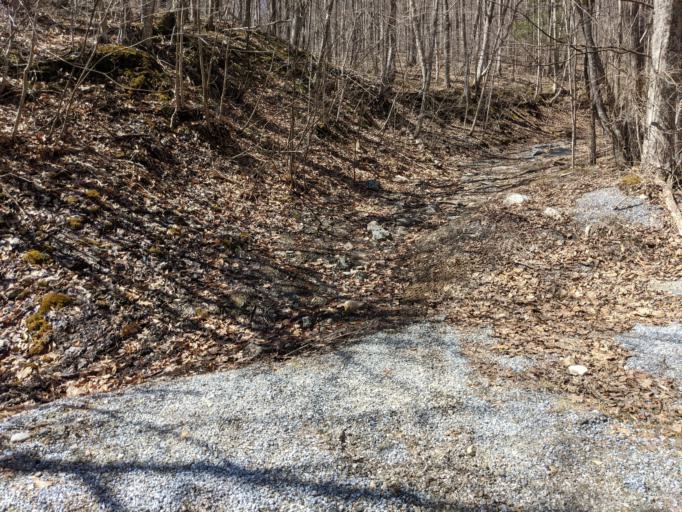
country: US
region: Vermont
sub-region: Bennington County
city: Manchester Center
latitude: 43.2411
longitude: -73.0130
